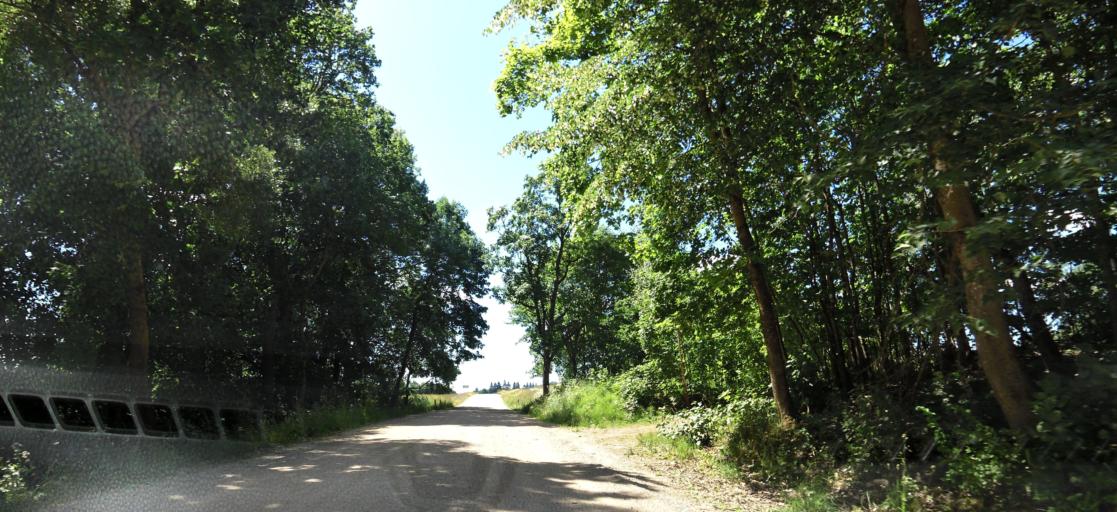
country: LT
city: Kupiskis
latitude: 55.9524
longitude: 24.9808
